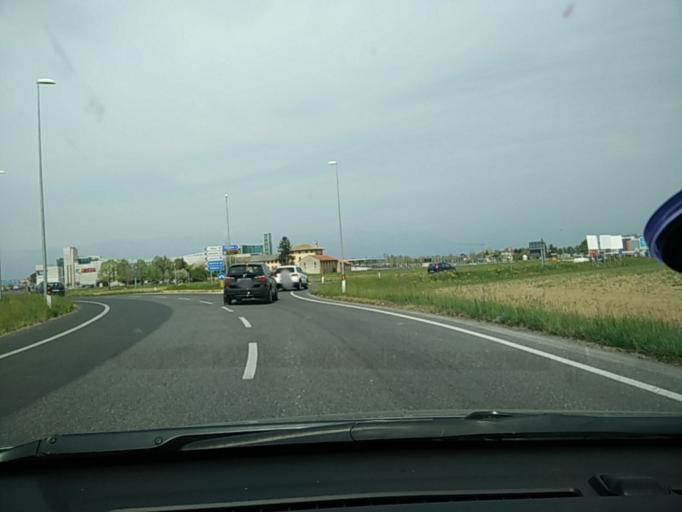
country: IT
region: Friuli Venezia Giulia
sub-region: Provincia di Pordenone
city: Pordenone
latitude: 45.9482
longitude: 12.6952
